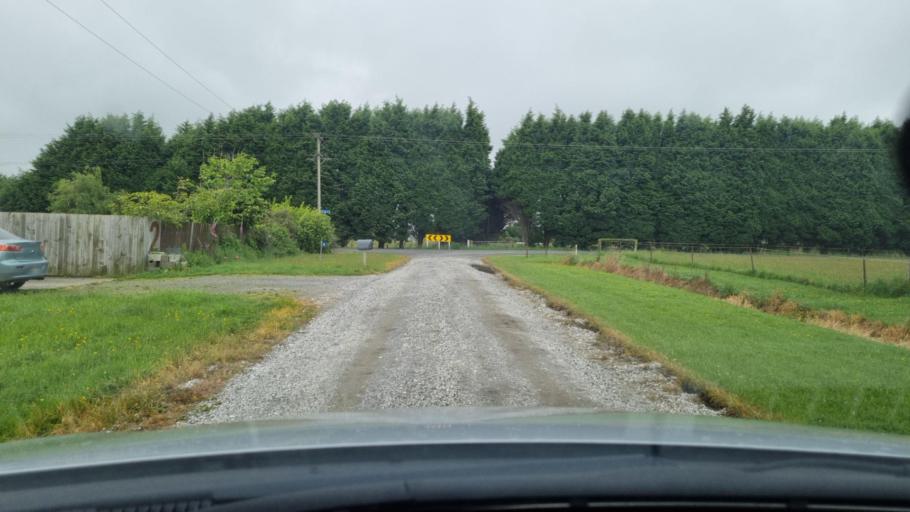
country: NZ
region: Southland
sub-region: Invercargill City
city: Invercargill
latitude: -46.4760
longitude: 168.3913
